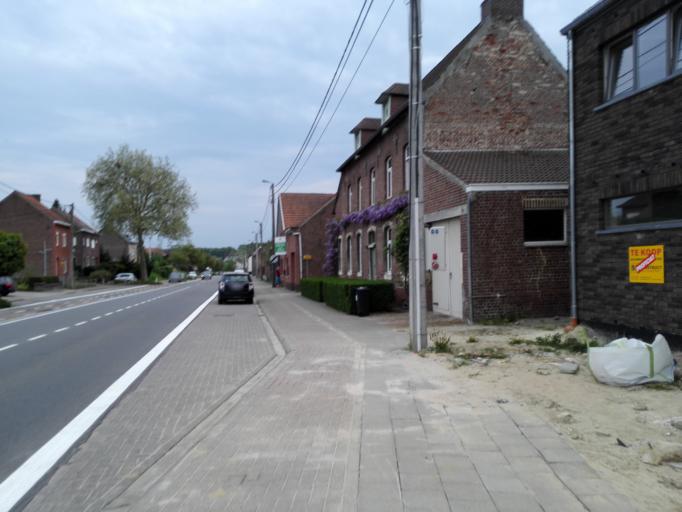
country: BE
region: Flanders
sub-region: Provincie Vlaams-Brabant
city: Oud-Heverlee
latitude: 50.8302
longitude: 4.7003
